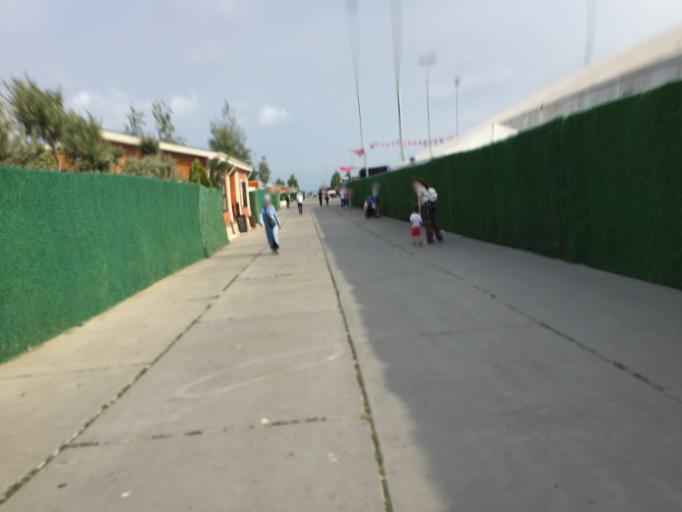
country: TR
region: Istanbul
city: Istanbul
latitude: 41.0010
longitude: 28.9394
